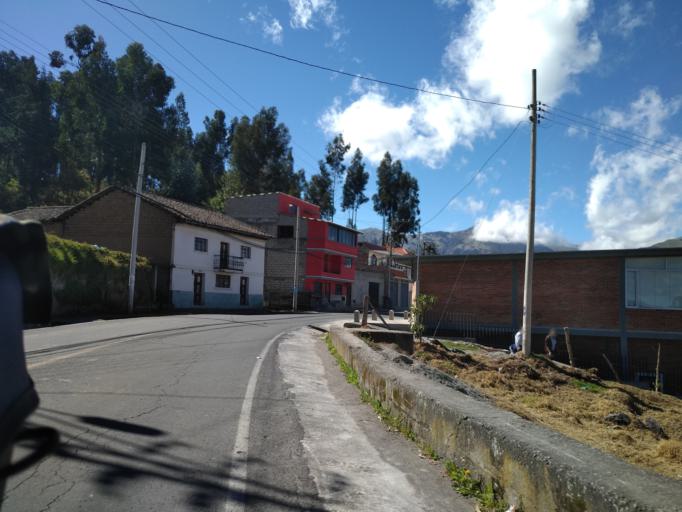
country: EC
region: Imbabura
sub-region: Canton Otavalo
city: Otavalo
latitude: 0.2107
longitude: -78.2088
